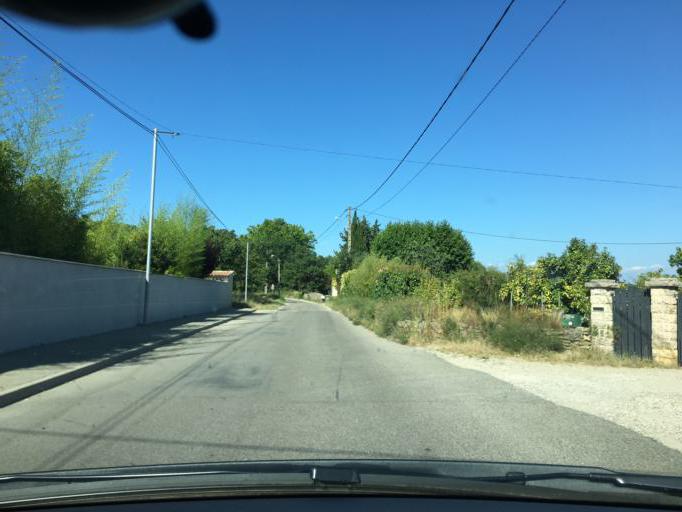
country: FR
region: Provence-Alpes-Cote d'Azur
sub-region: Departement du Vaucluse
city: Bollene
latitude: 44.3029
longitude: 4.7563
